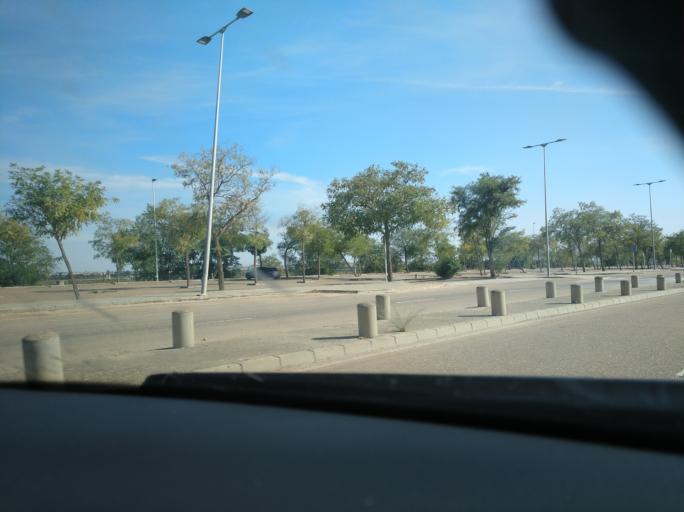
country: ES
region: Extremadura
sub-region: Provincia de Badajoz
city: Badajoz
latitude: 38.8806
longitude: -7.0254
